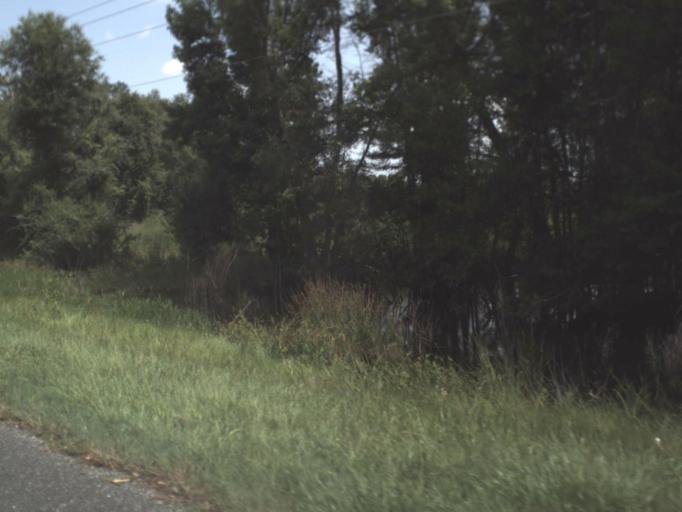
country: US
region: Florida
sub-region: Taylor County
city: Perry
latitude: 29.9701
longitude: -83.4789
